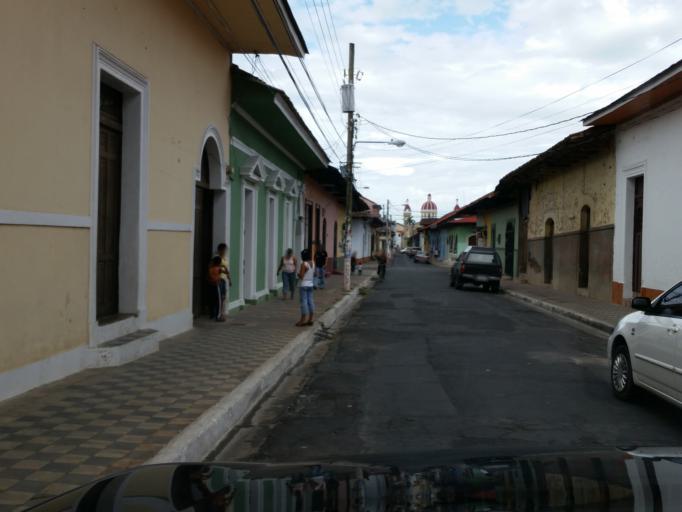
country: NI
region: Granada
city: Granada
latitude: 11.9300
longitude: -85.9580
